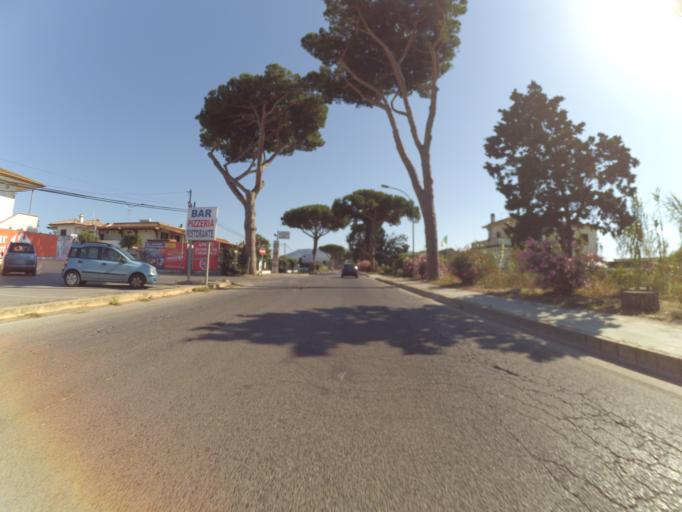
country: IT
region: Latium
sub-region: Provincia di Latina
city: San Felice Circeo
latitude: 41.2719
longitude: 13.0983
